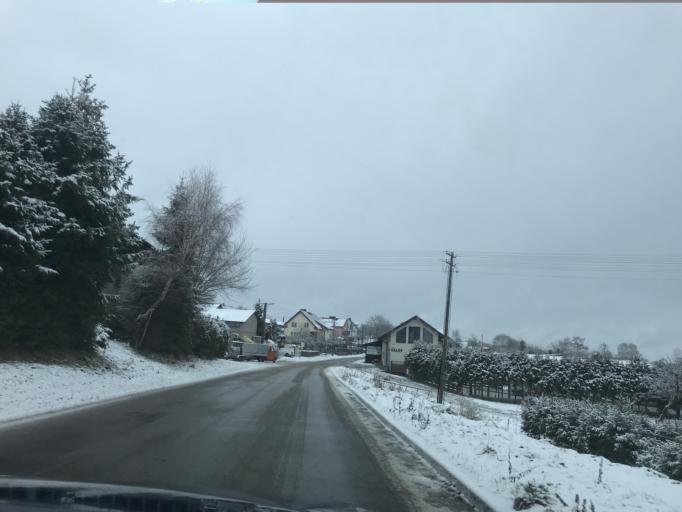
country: PL
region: Pomeranian Voivodeship
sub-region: Powiat bytowski
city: Bytow
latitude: 54.2158
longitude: 17.5616
